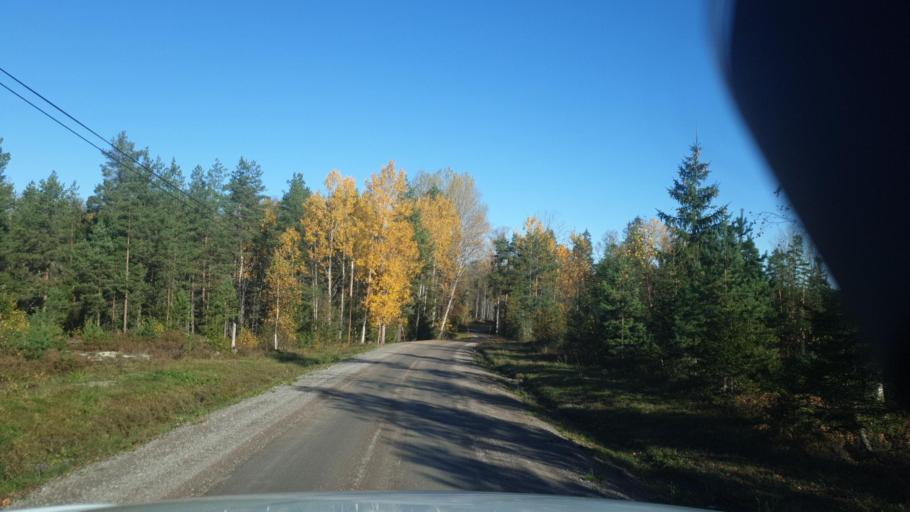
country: SE
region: Vaermland
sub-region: Arvika Kommun
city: Arvika
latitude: 59.5251
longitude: 12.7355
